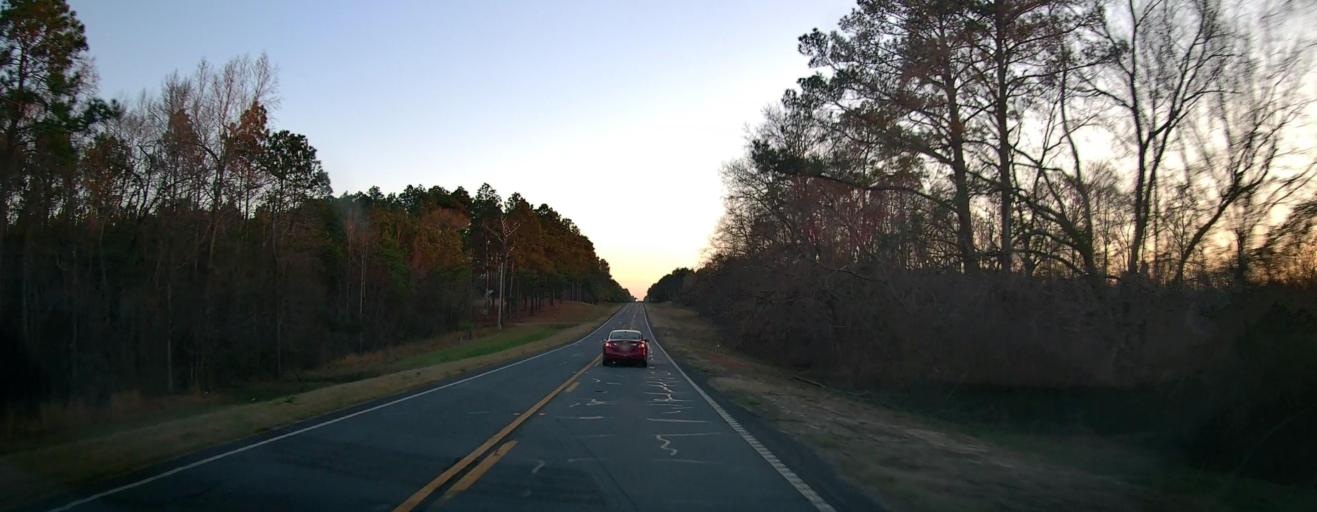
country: US
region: Georgia
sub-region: Dodge County
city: Eastman
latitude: 32.2263
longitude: -83.1540
